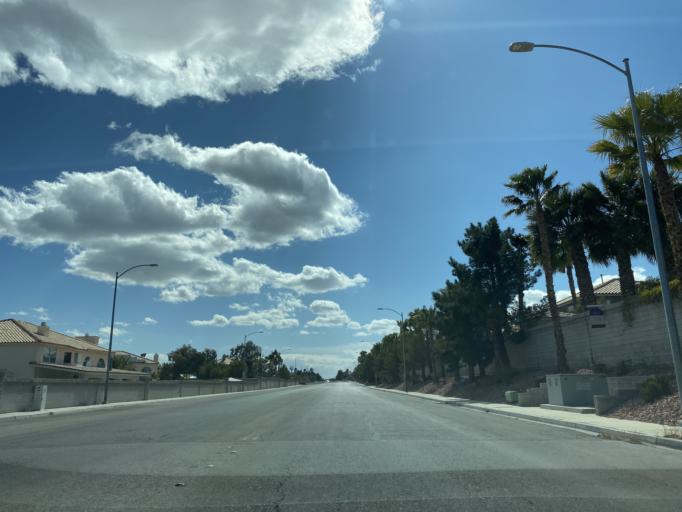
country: US
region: Nevada
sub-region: Clark County
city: Summerlin South
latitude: 36.2367
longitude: -115.2884
